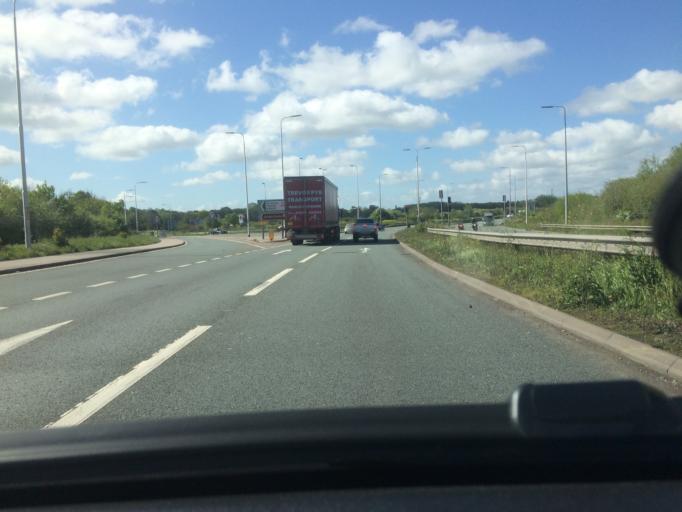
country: GB
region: England
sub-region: Cheshire West and Chester
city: Eccleston
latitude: 53.1520
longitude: -2.9162
